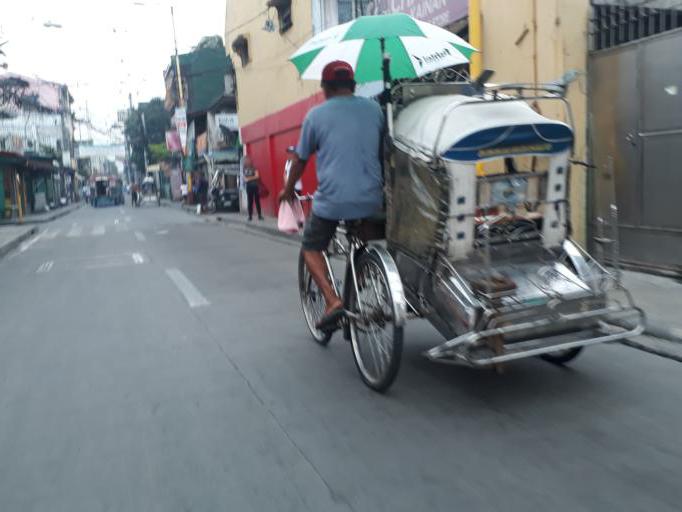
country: PH
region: Calabarzon
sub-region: Province of Rizal
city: Navotas
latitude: 14.6580
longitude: 120.9458
